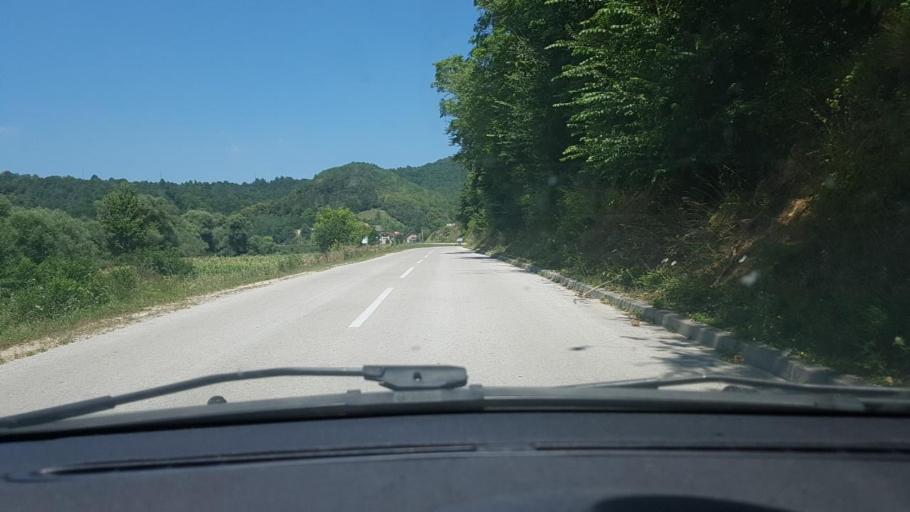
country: BA
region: Federation of Bosnia and Herzegovina
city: Orasac
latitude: 44.5619
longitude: 16.1019
